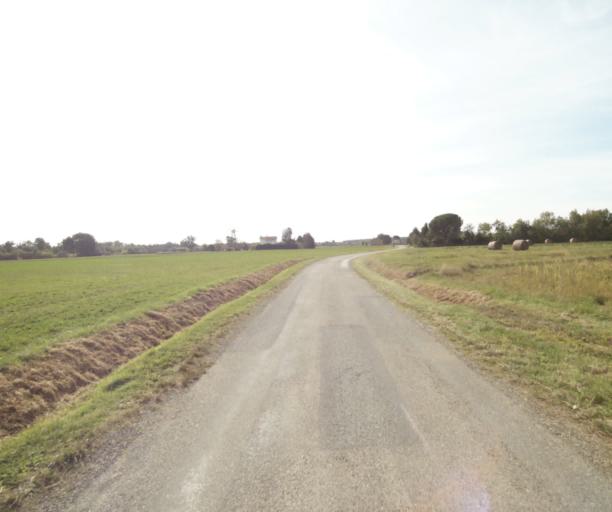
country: FR
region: Midi-Pyrenees
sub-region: Departement du Tarn-et-Garonne
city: Campsas
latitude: 43.8868
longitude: 1.3540
